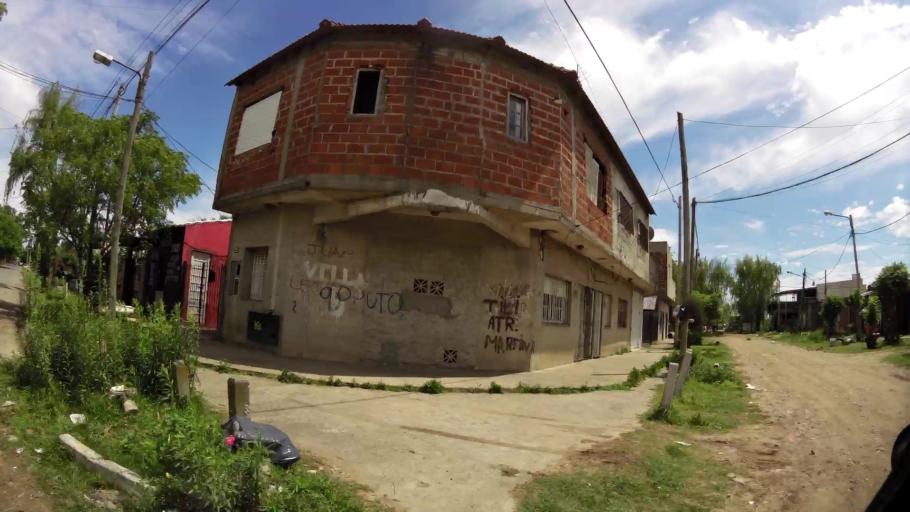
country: AR
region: Buenos Aires
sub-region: Partido de Quilmes
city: Quilmes
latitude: -34.7749
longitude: -58.2568
